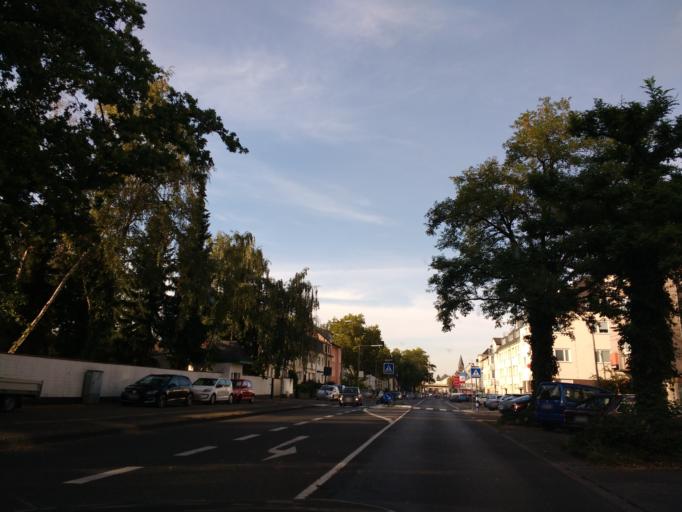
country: DE
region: North Rhine-Westphalia
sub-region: Regierungsbezirk Koln
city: Nippes
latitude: 50.9813
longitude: 6.9606
